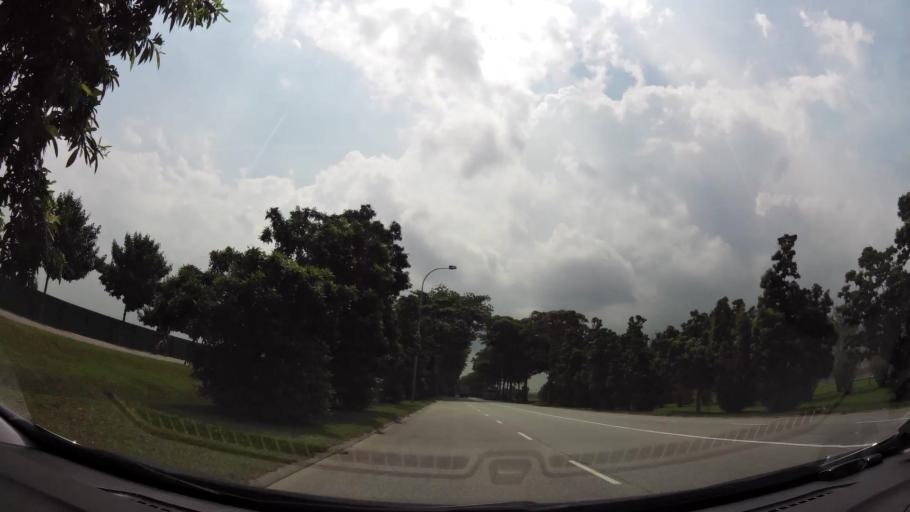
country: MY
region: Johor
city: Kampung Pasir Gudang Baru
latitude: 1.3613
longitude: 104.0017
